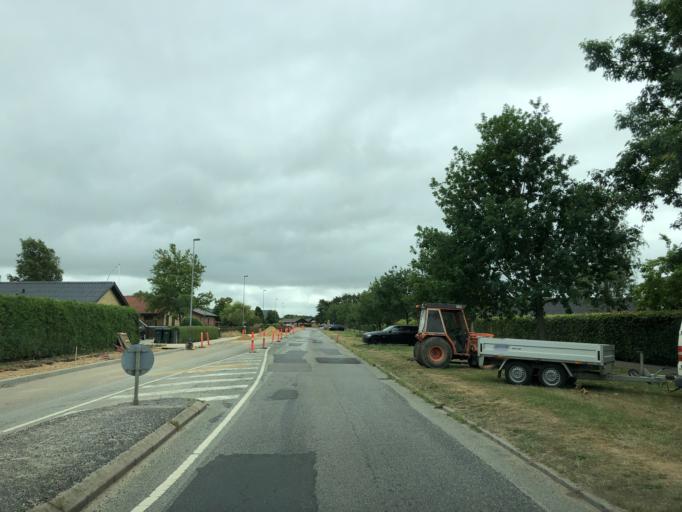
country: DK
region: Central Jutland
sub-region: Herning Kommune
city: Vildbjerg
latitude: 56.1963
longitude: 8.7599
